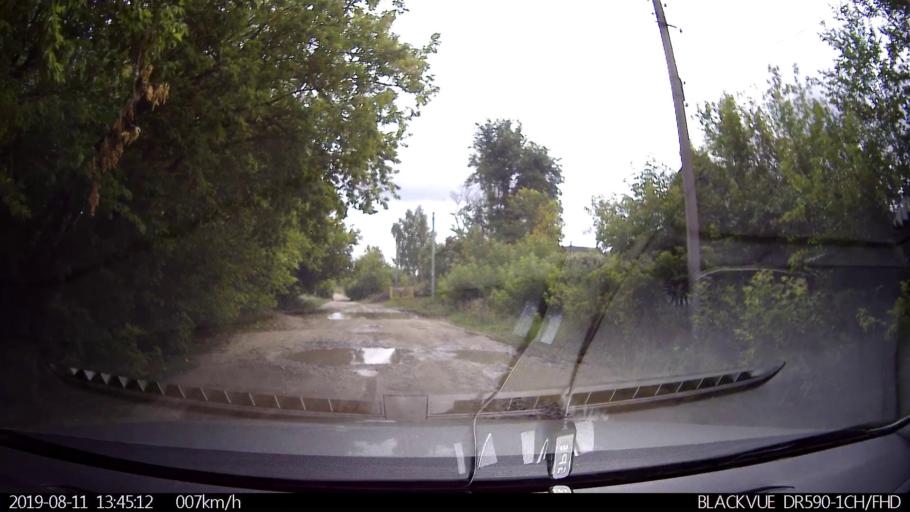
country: RU
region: Ulyanovsk
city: Ignatovka
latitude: 53.8525
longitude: 47.5747
